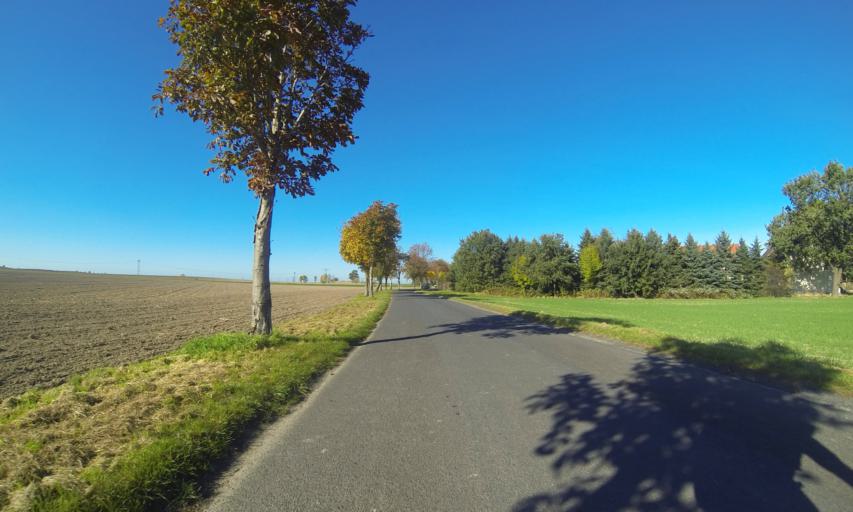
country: DE
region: Saxony
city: Weinbohla
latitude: 51.2190
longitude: 13.5930
